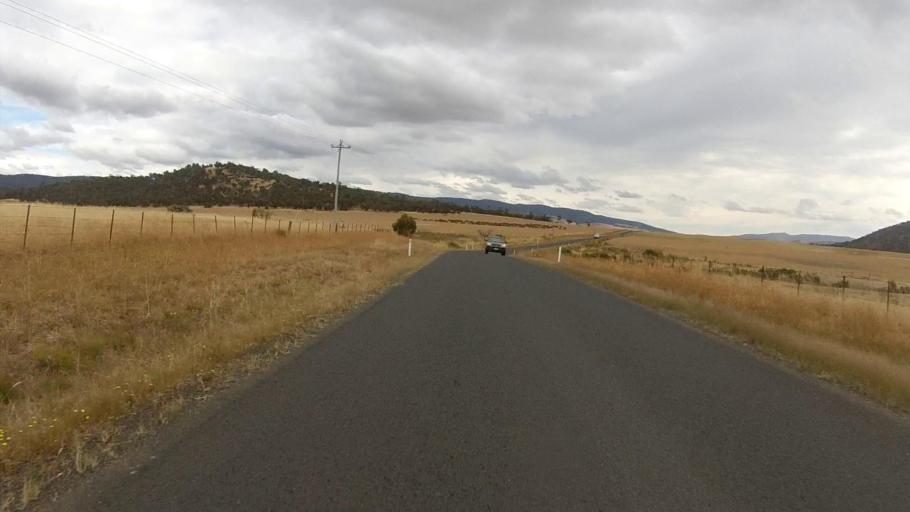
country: AU
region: Tasmania
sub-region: Northern Midlands
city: Evandale
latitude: -41.8246
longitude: 147.8083
